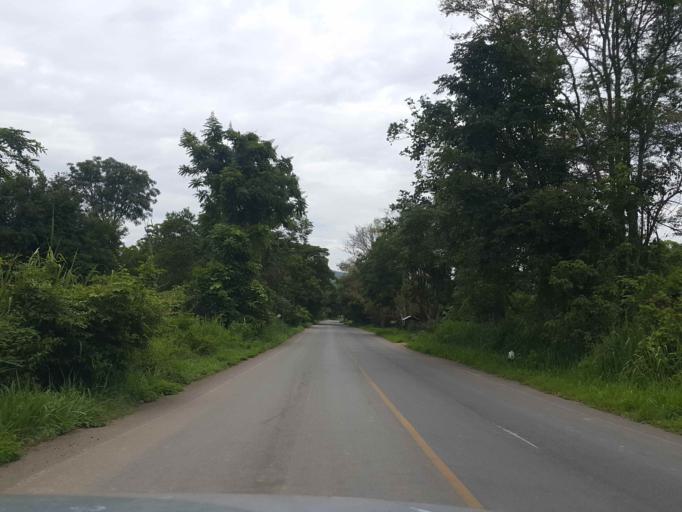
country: TH
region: Lampang
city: Thoen
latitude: 17.5660
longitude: 99.3309
